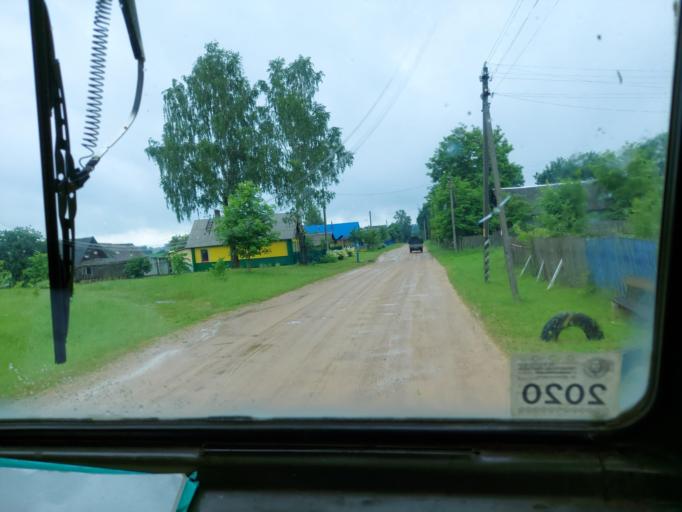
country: BY
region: Mogilev
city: Poselok Voskhod
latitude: 53.6810
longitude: 30.3879
